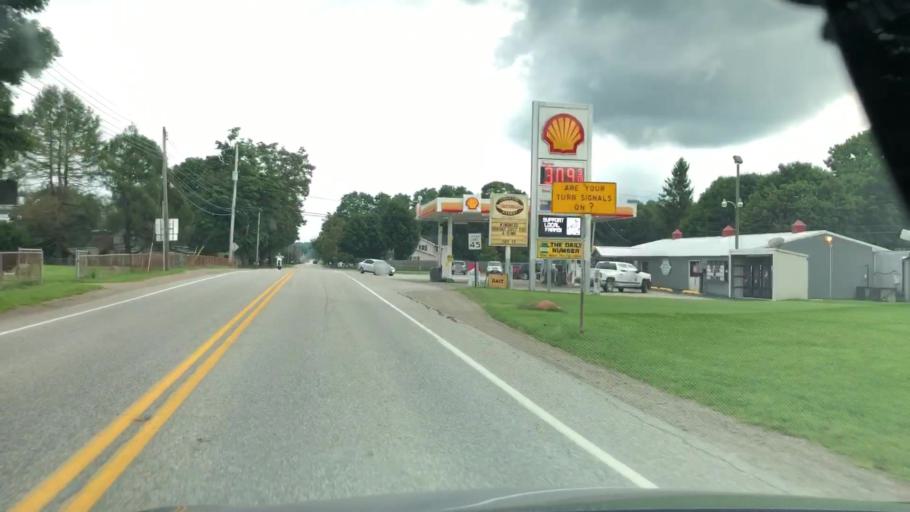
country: US
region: Pennsylvania
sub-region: Erie County
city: Union City
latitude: 42.0238
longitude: -79.8180
